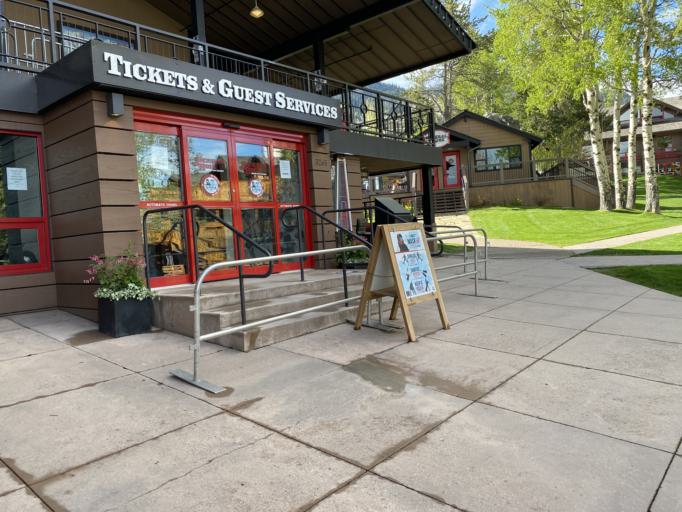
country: US
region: Wyoming
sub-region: Teton County
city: Moose Wilson Road
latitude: 43.5876
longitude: -110.8276
